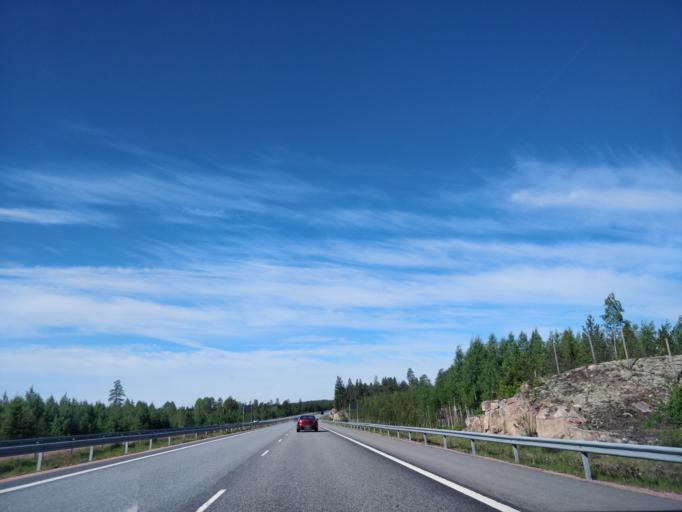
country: FI
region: Varsinais-Suomi
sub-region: Salo
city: Muurla
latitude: 60.3764
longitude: 23.4055
